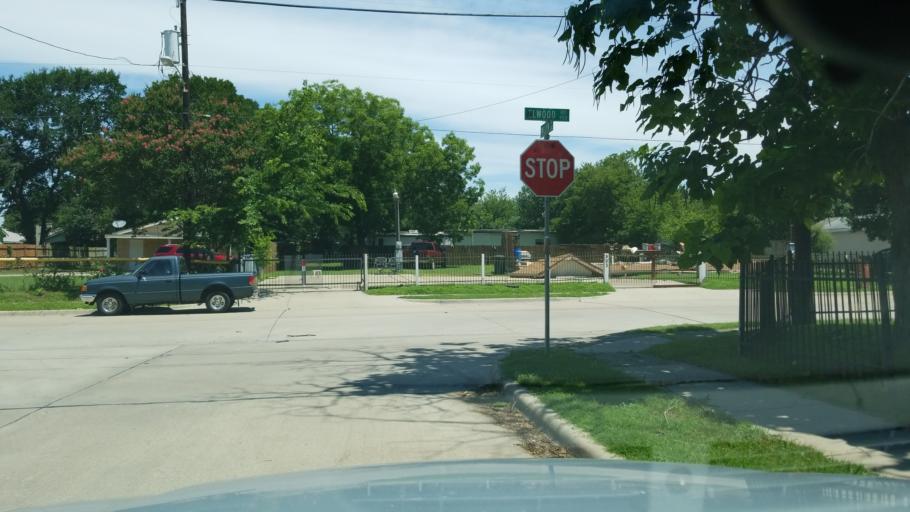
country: US
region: Texas
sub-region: Dallas County
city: Irving
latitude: 32.8199
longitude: -96.9359
